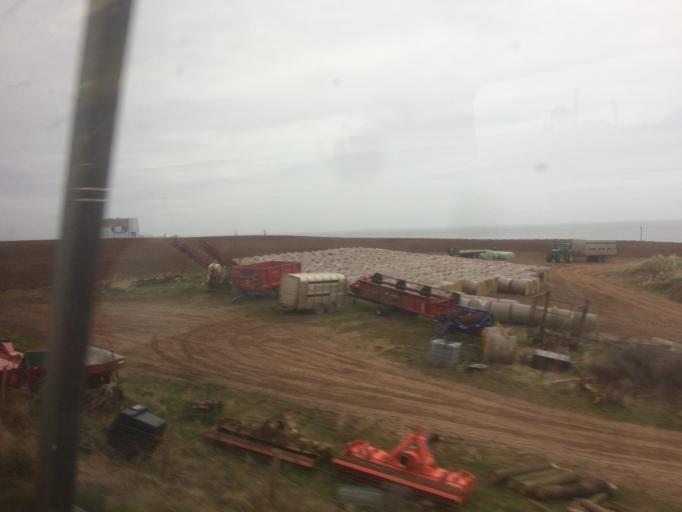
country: GB
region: Scotland
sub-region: East Lothian
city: Dunbar
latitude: 55.9543
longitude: -2.3978
